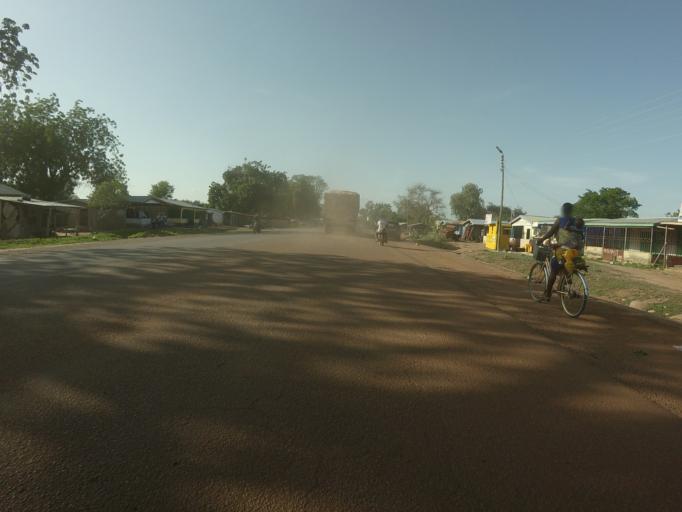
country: GH
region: Upper East
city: Navrongo
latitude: 10.9053
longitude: -1.0912
